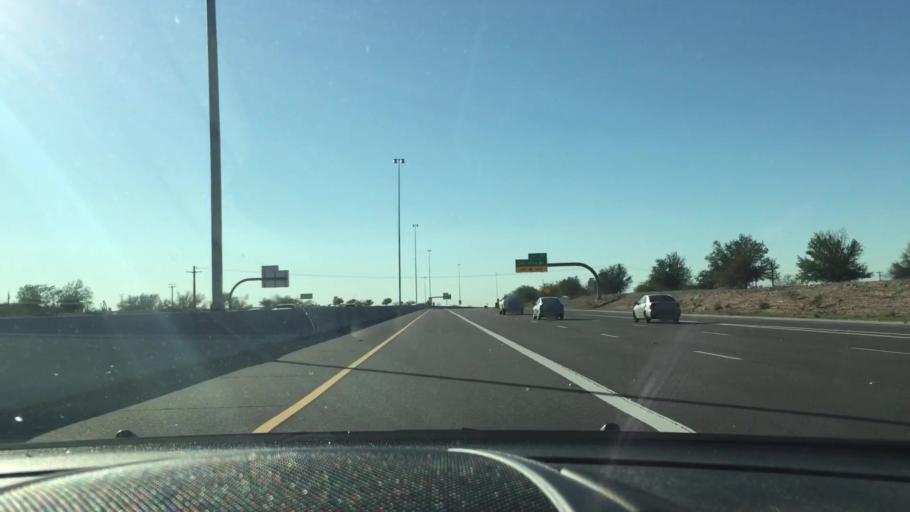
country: US
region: Arizona
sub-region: Maricopa County
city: Mesa
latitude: 33.4793
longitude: -111.7417
